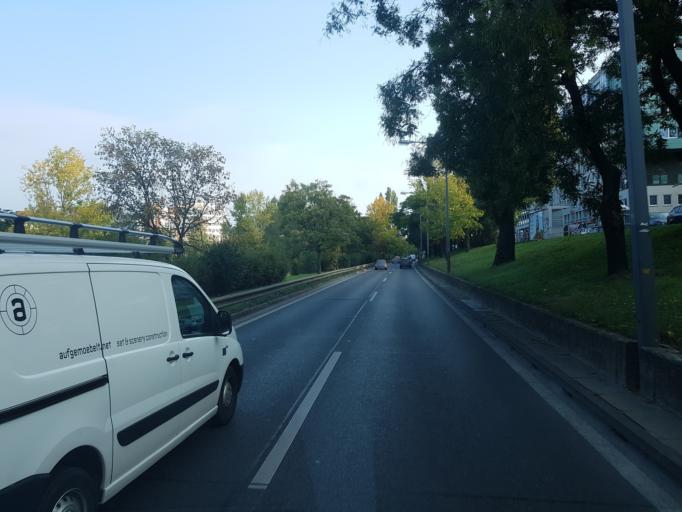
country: AT
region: Vienna
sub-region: Wien Stadt
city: Vienna
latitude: 48.2401
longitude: 16.3647
